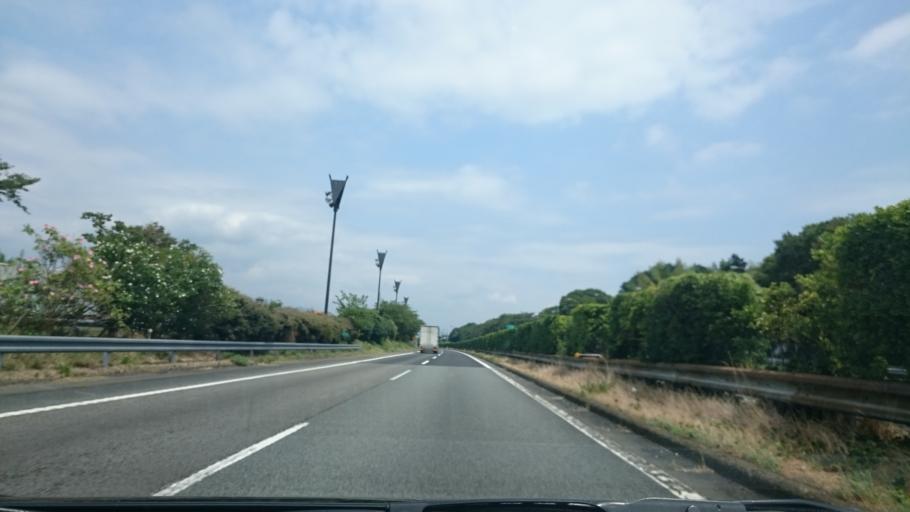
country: JP
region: Shizuoka
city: Shizuoka-shi
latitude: 34.9826
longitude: 138.4335
